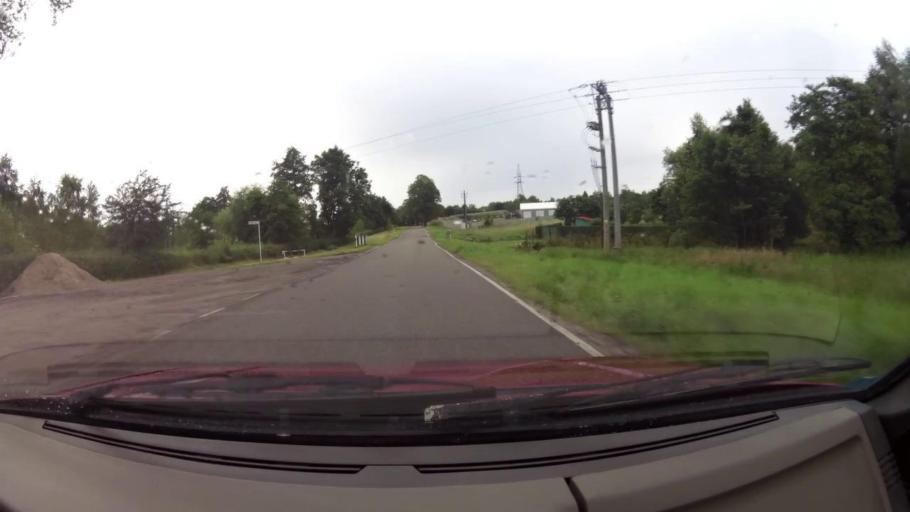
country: PL
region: West Pomeranian Voivodeship
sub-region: Powiat swidwinski
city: Swidwin
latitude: 53.7562
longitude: 15.7642
